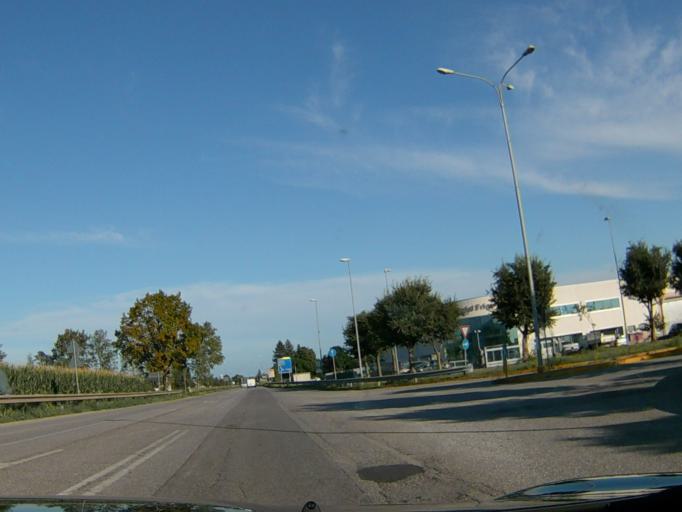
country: IT
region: Lombardy
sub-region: Provincia di Brescia
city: Ponte San Marco
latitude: 45.4732
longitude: 10.4313
